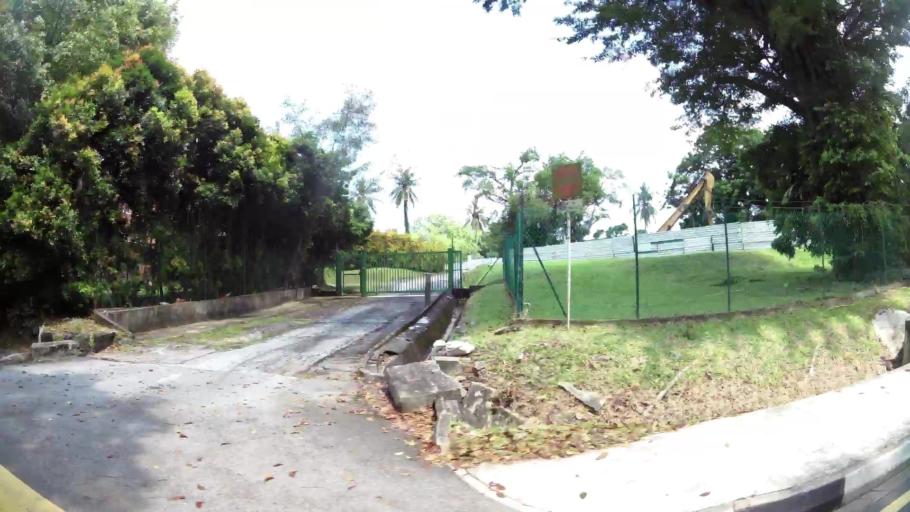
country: SG
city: Singapore
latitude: 1.3323
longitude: 103.7948
